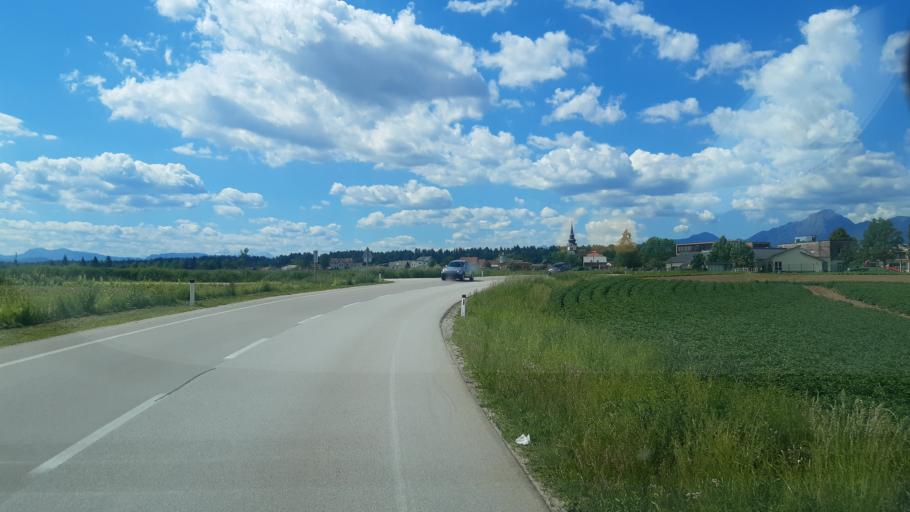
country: SI
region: Vodice
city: Vodice
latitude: 46.1829
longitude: 14.4977
